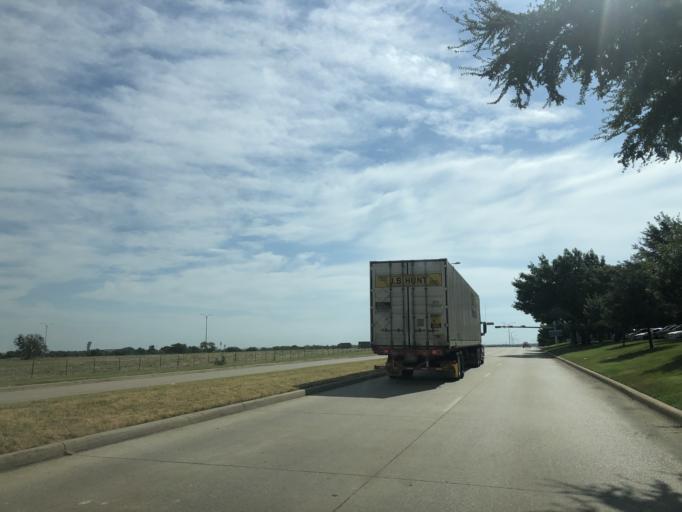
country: US
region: Texas
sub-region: Tarrant County
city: Haslet
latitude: 32.9739
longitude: -97.3296
